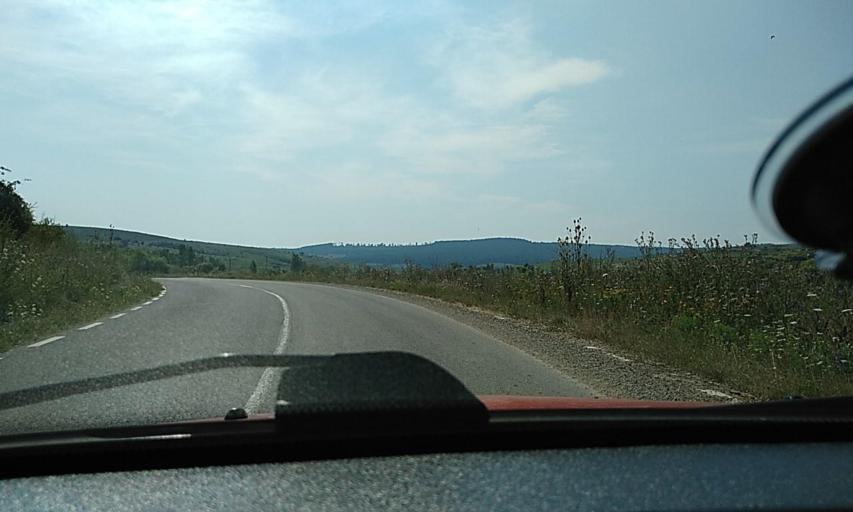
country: RO
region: Brasov
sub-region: Oras Rupea
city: Fiser
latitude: 46.0305
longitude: 25.1417
